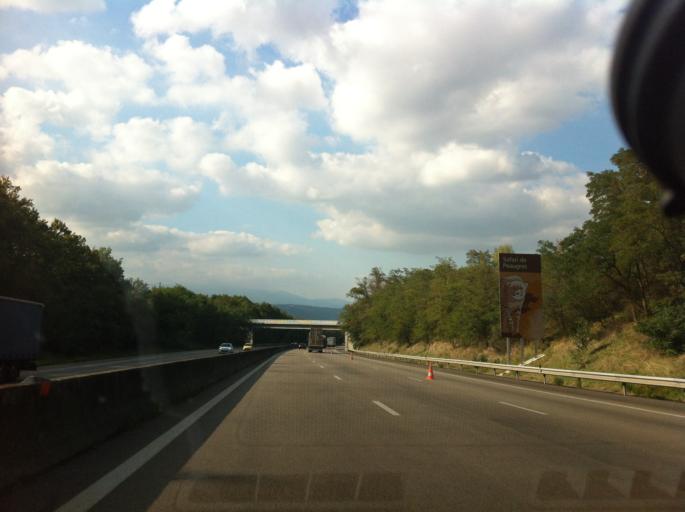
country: FR
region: Rhone-Alpes
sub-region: Departement de la Drome
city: Beausemblant
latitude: 45.2279
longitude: 4.8532
